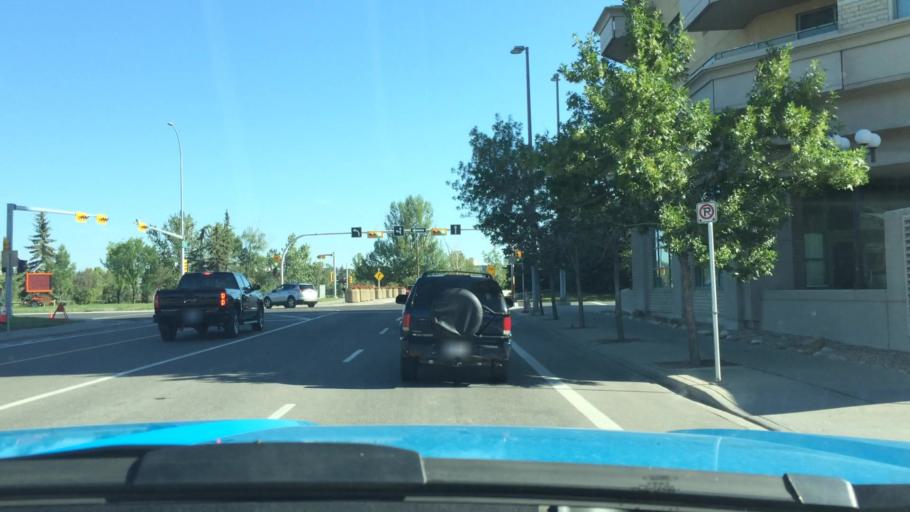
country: CA
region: Alberta
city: Calgary
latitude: 51.0476
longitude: -114.0885
